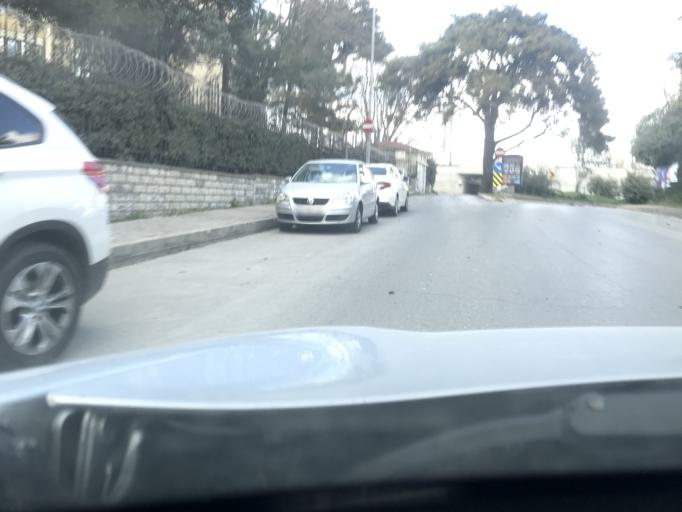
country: TR
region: Istanbul
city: Bahcelievler
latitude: 40.9623
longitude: 28.8175
